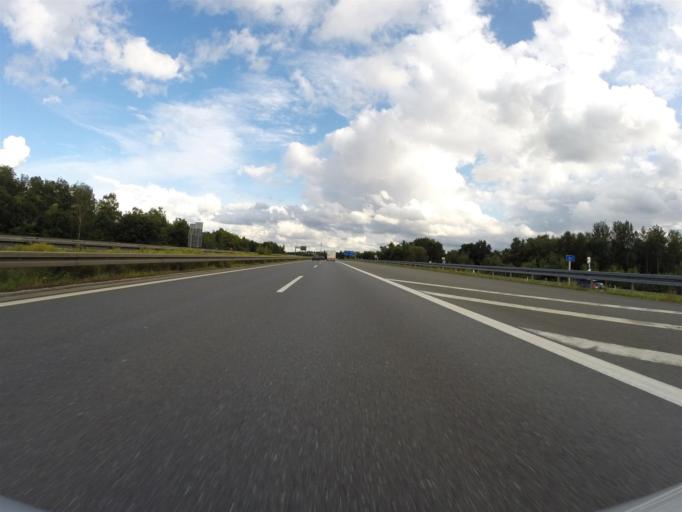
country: DE
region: Bavaria
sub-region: Regierungsbezirk Mittelfranken
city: Wendelstein
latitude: 49.3790
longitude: 11.1345
